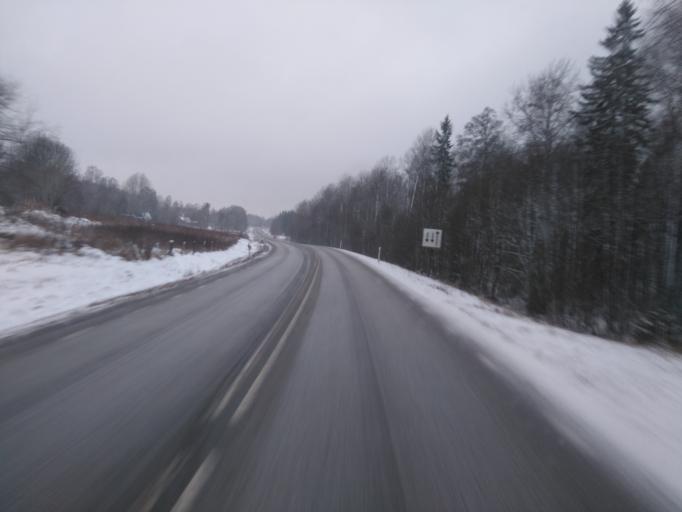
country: SE
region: Joenkoeping
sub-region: Eksjo Kommun
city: Eksjoe
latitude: 57.6370
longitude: 15.0973
